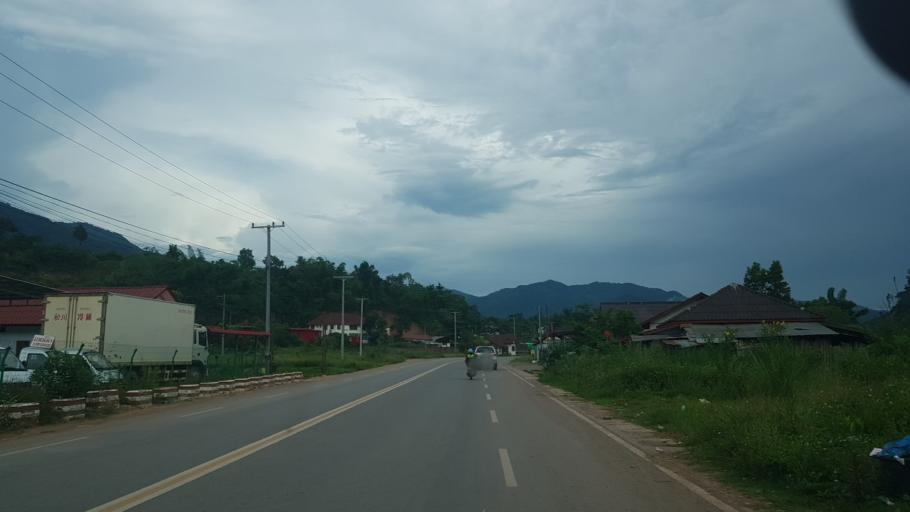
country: LA
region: Oudomxai
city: Muang Xay
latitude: 20.6562
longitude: 101.9769
